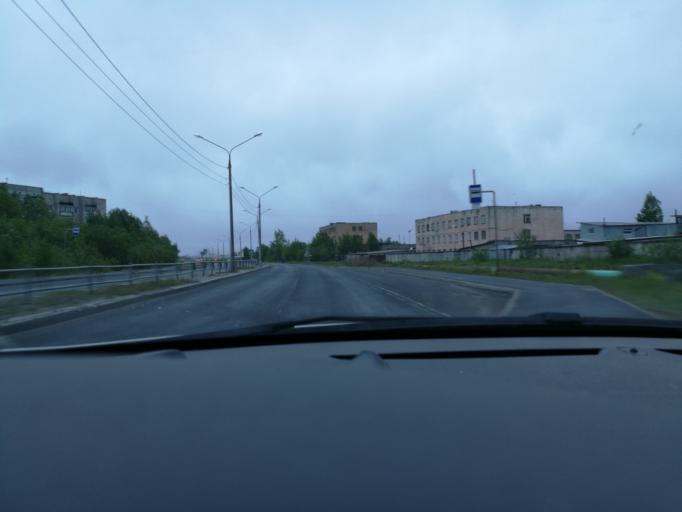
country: RU
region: Arkhangelskaya
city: Severodvinsk
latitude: 64.5663
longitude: 39.7868
